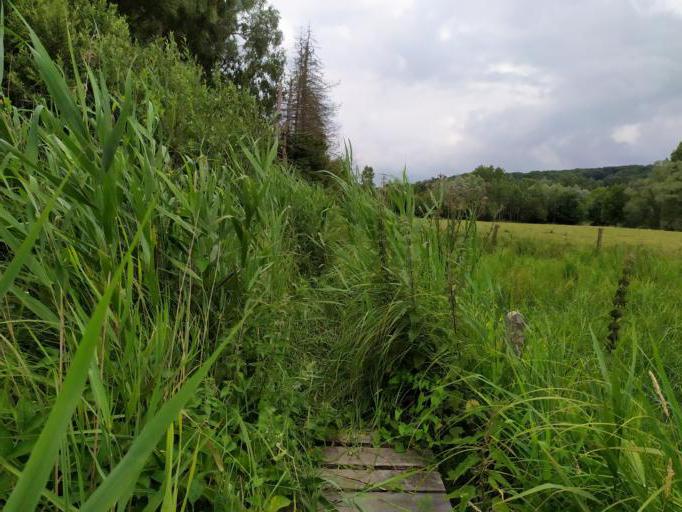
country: BE
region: Wallonia
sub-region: Province du Brabant Wallon
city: Grez-Doiceau
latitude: 50.7621
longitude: 4.6474
